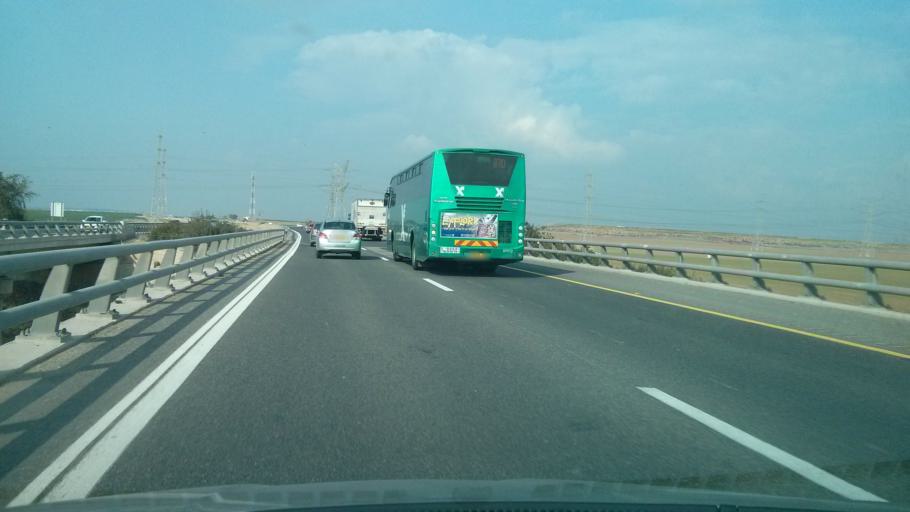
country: IL
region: Central District
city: Bene 'Ayish
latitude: 31.7080
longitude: 34.8202
